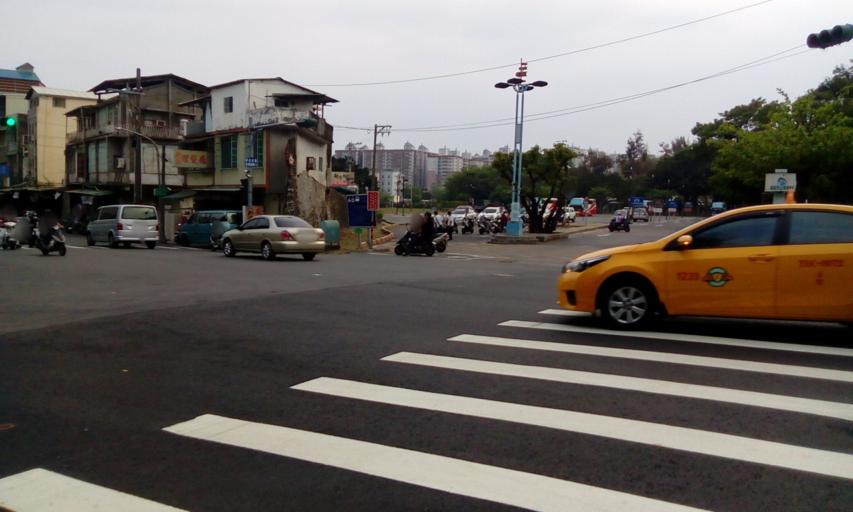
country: TW
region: Kaohsiung
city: Kaohsiung
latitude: 22.6790
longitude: 120.2926
